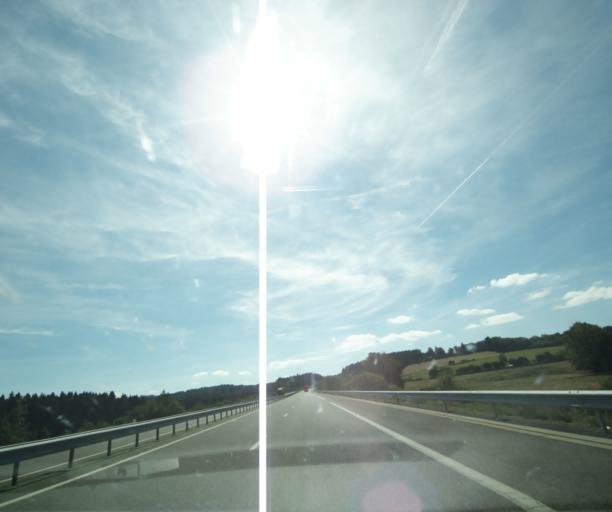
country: FR
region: Auvergne
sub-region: Departement du Puy-de-Dome
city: Gelles
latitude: 45.7650
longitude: 2.7301
